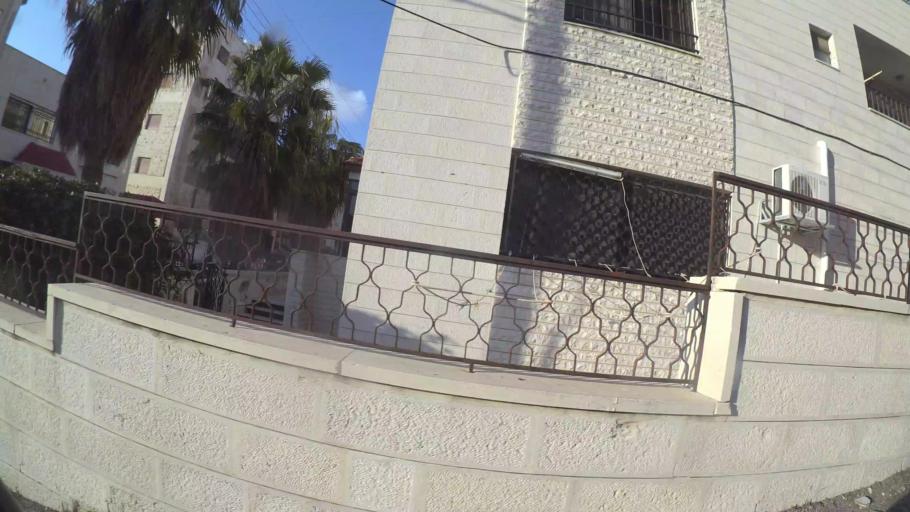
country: JO
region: Amman
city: Al Jubayhah
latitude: 31.9953
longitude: 35.8671
